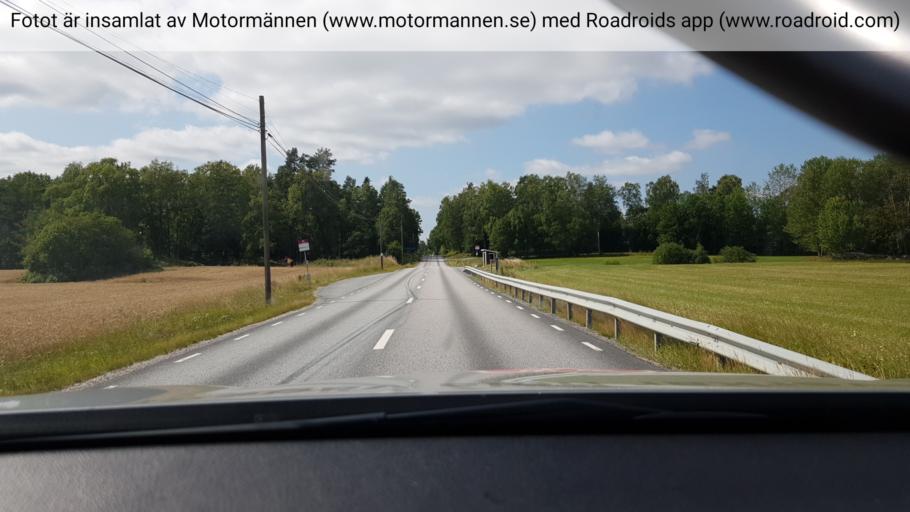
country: SE
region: Stockholm
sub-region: Osterakers Kommun
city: Akersberga
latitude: 59.5502
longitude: 18.2079
